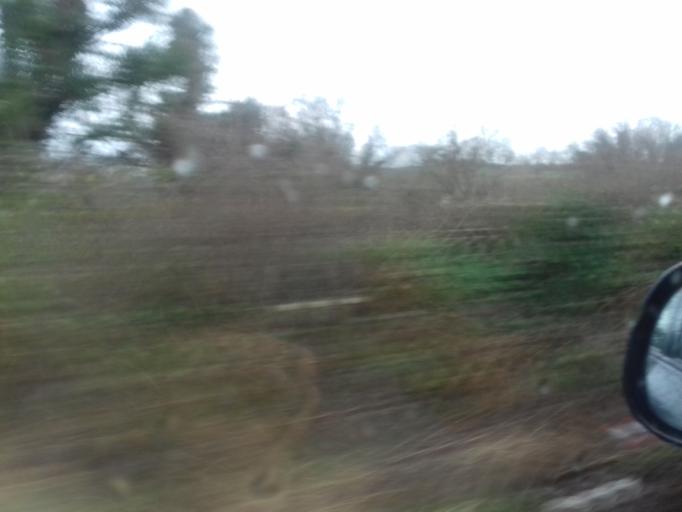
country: IE
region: Leinster
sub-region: Kilkenny
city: Graiguenamanagh
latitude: 52.5808
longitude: -6.9529
